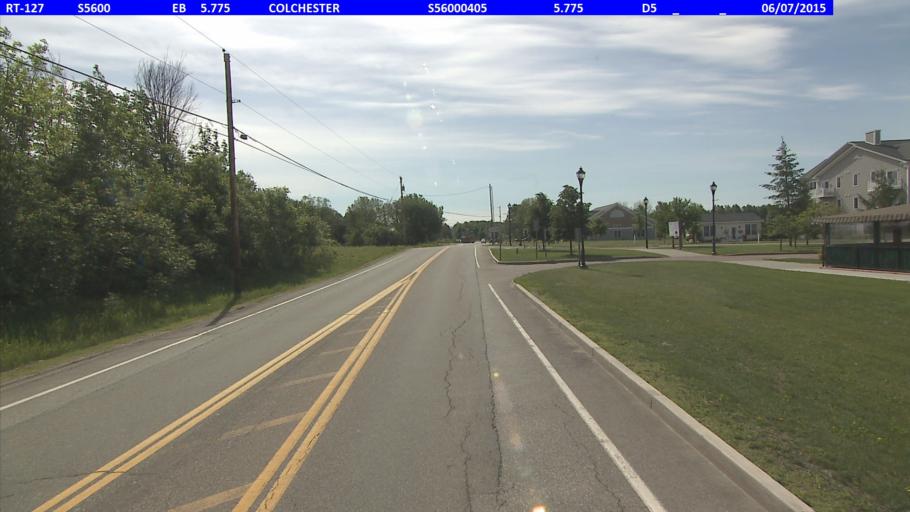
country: US
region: Vermont
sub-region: Chittenden County
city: Colchester
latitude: 44.5301
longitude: -73.1746
